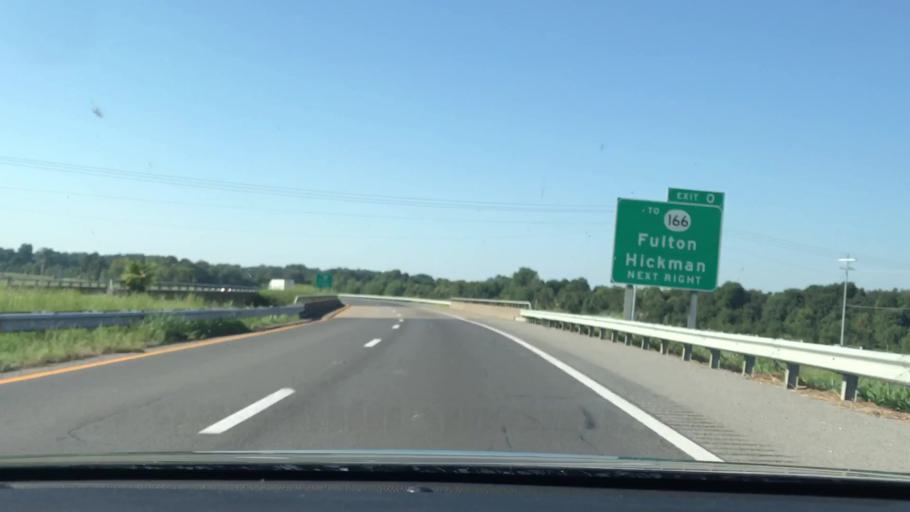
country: US
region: Kentucky
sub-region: Fulton County
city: Fulton
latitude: 36.5161
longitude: -88.8985
